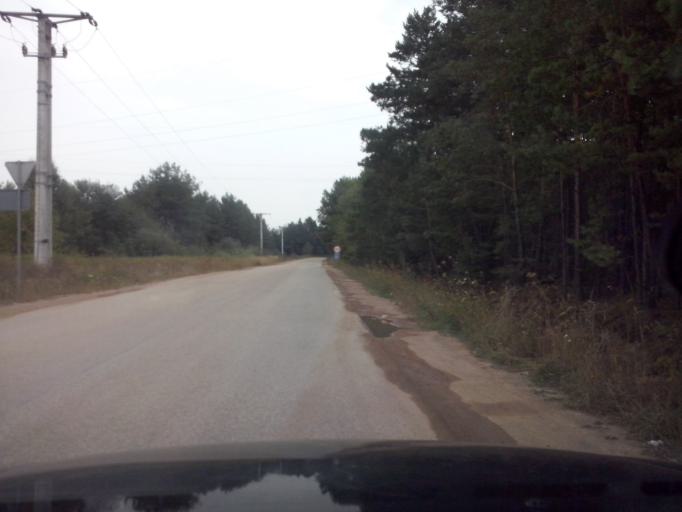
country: PL
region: Swietokrzyskie
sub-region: Kielce
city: Osiedle-Nowiny
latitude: 50.7812
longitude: 20.5305
